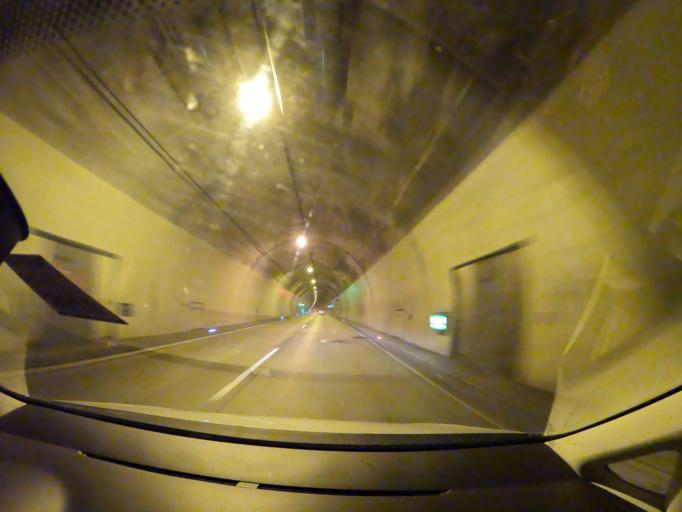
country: AT
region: Styria
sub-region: Politischer Bezirk Voitsberg
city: Modriach
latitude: 46.9636
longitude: 15.0658
